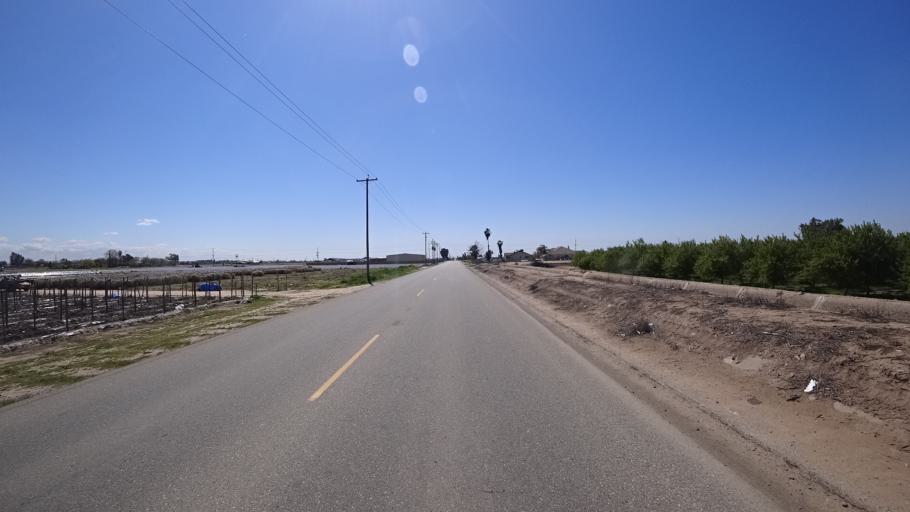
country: US
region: California
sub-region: Fresno County
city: West Park
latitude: 36.7095
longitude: -119.8445
